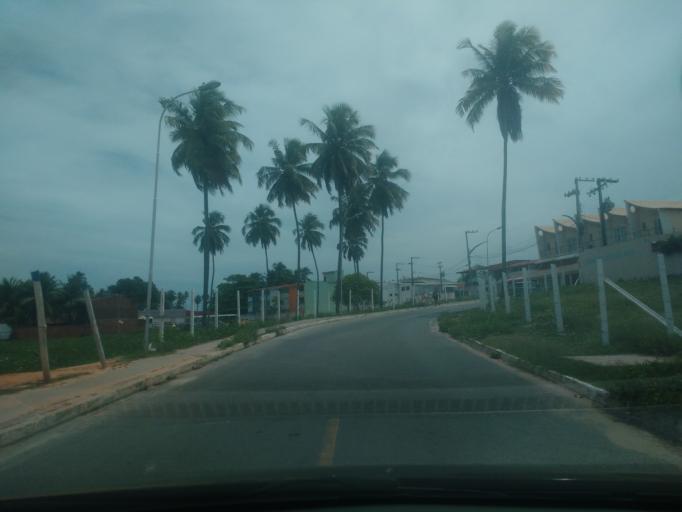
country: BR
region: Alagoas
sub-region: Marechal Deodoro
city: Marechal Deodoro
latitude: -9.7686
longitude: -35.8433
